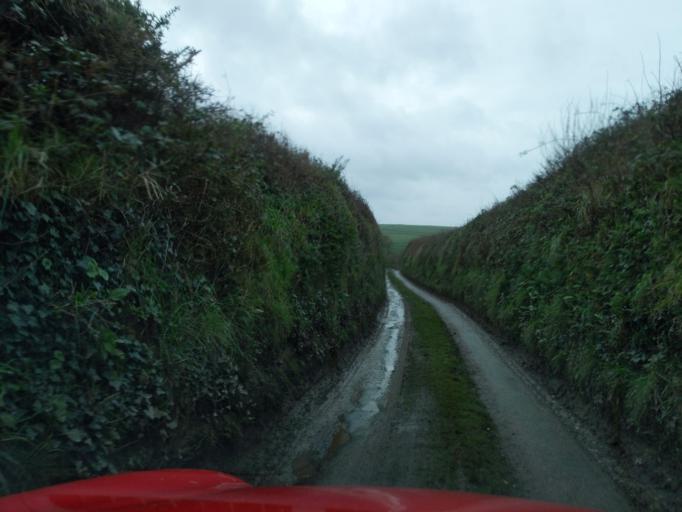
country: GB
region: England
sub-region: Cornwall
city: Fowey
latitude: 50.3408
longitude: -4.5749
